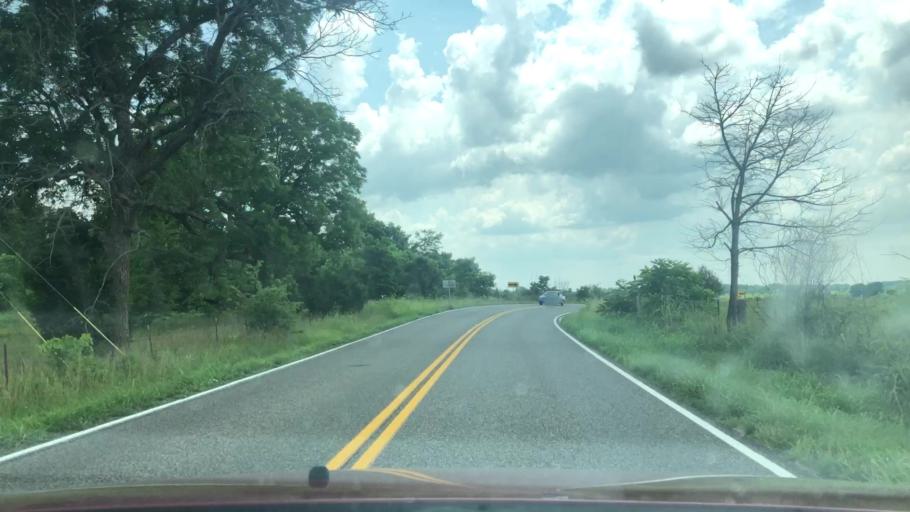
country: US
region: Missouri
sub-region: Christian County
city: Ozark
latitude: 36.9416
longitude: -93.2515
